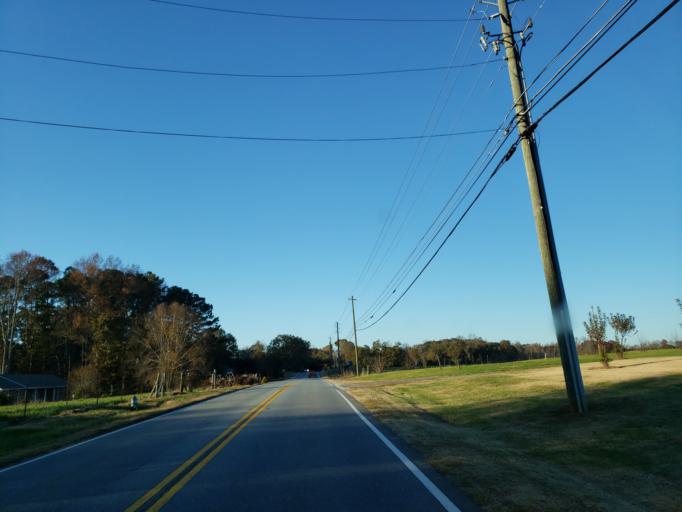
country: US
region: Georgia
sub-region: Cherokee County
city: Holly Springs
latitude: 34.1847
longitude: -84.4213
